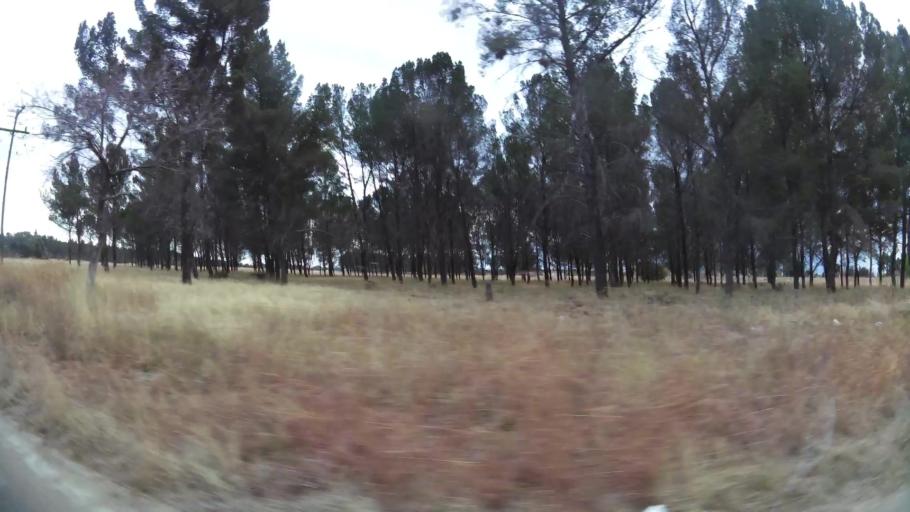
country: ZA
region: Orange Free State
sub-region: Lejweleputswa District Municipality
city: Welkom
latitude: -27.9699
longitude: 26.7008
